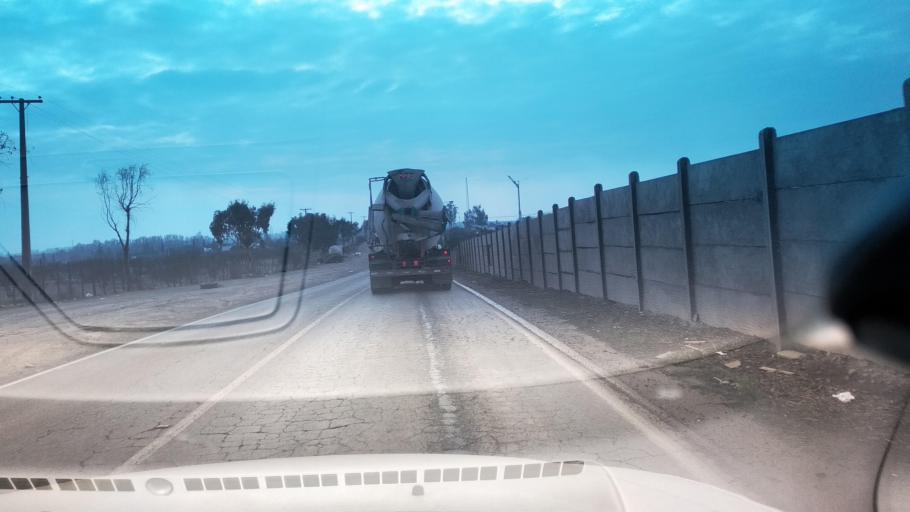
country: CL
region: Santiago Metropolitan
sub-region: Provincia de Santiago
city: Lo Prado
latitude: -33.4476
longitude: -70.7997
